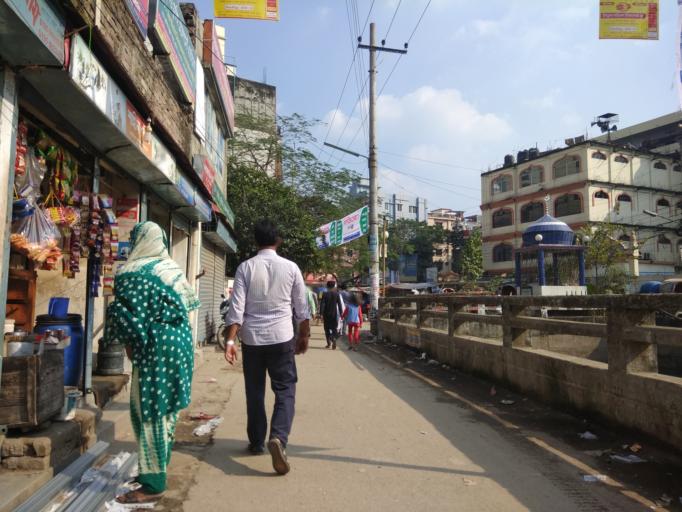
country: BD
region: Dhaka
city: Azimpur
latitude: 23.7618
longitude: 90.3552
